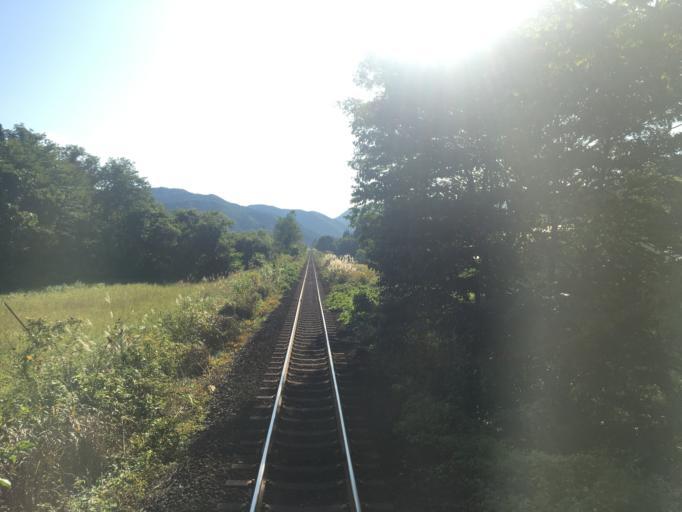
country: JP
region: Akita
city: Kakunodatemachi
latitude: 39.7485
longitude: 140.5955
